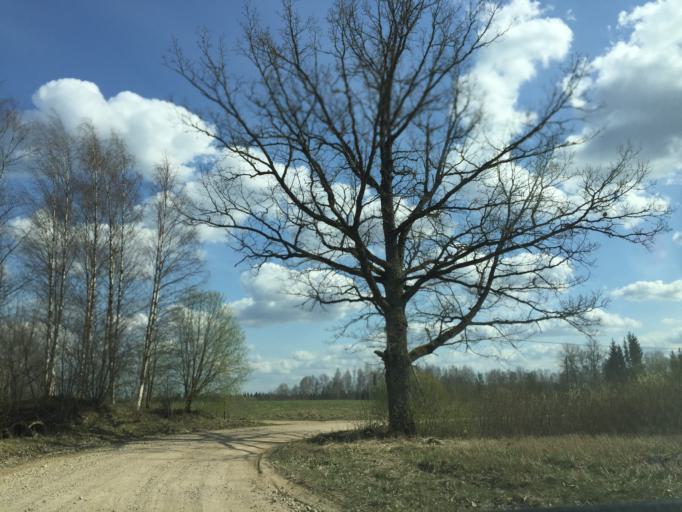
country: LV
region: Skriveri
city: Skriveri
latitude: 56.7763
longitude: 25.1974
